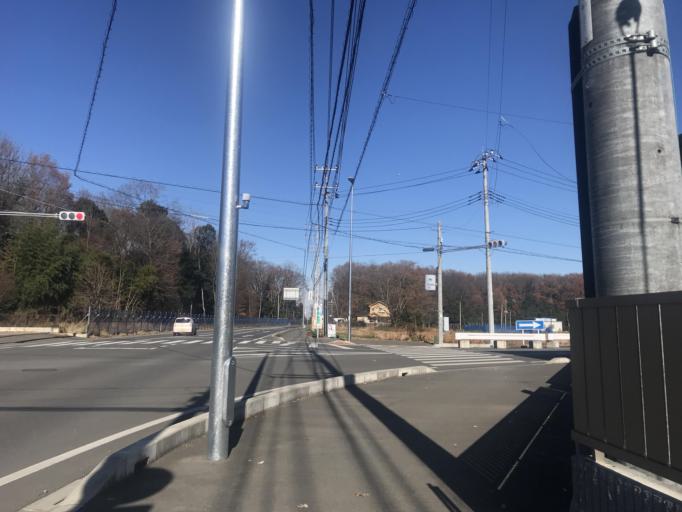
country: JP
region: Ibaraki
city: Yuki
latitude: 36.3409
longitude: 139.8789
